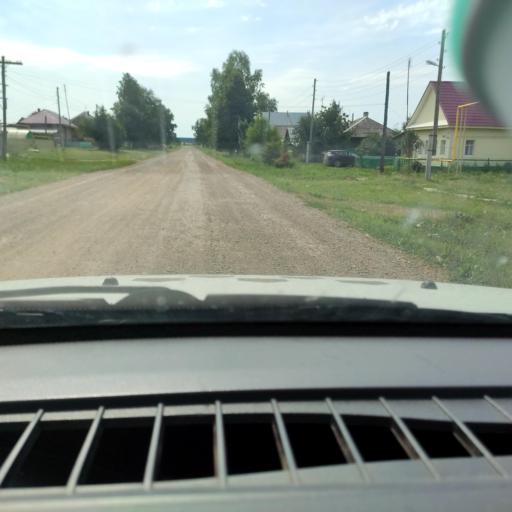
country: RU
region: Perm
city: Uinskoye
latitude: 57.1156
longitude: 56.5196
